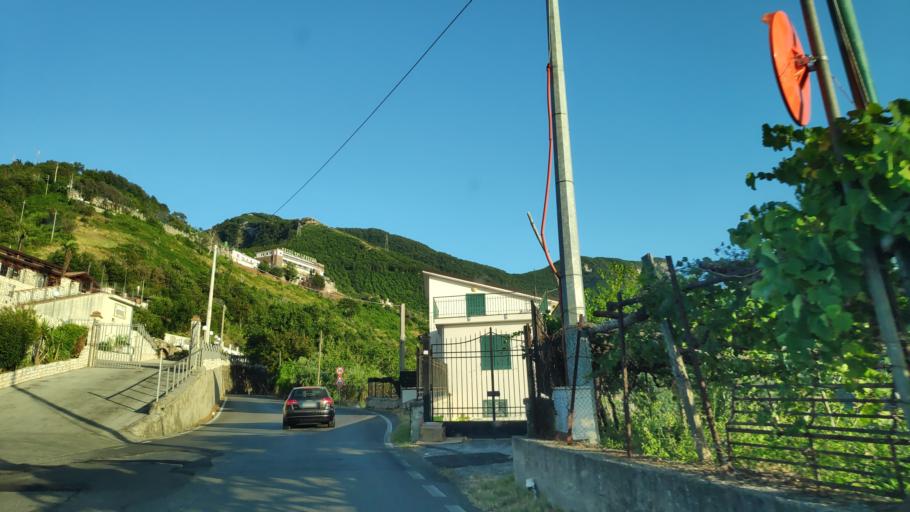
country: IT
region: Campania
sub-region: Provincia di Salerno
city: Corbara
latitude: 40.7268
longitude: 14.5979
